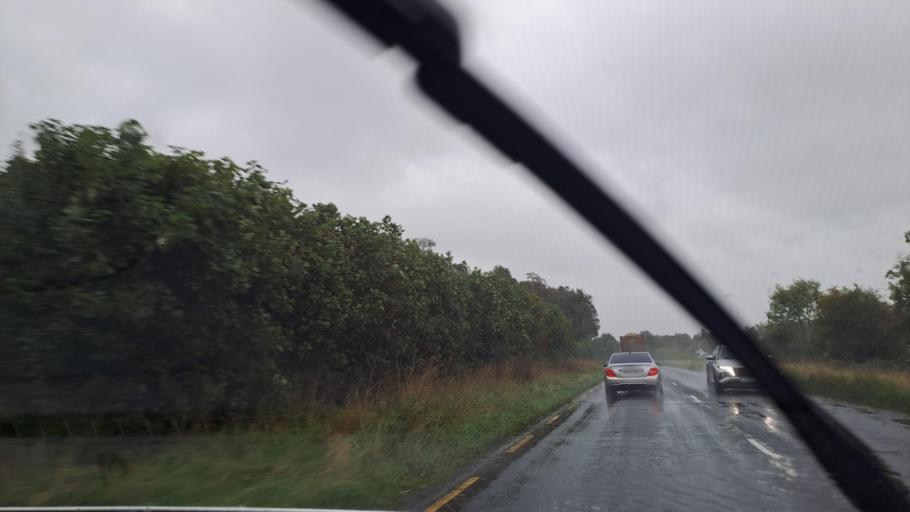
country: IE
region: Ulster
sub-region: County Monaghan
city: Carrickmacross
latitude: 53.9709
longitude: -6.6860
